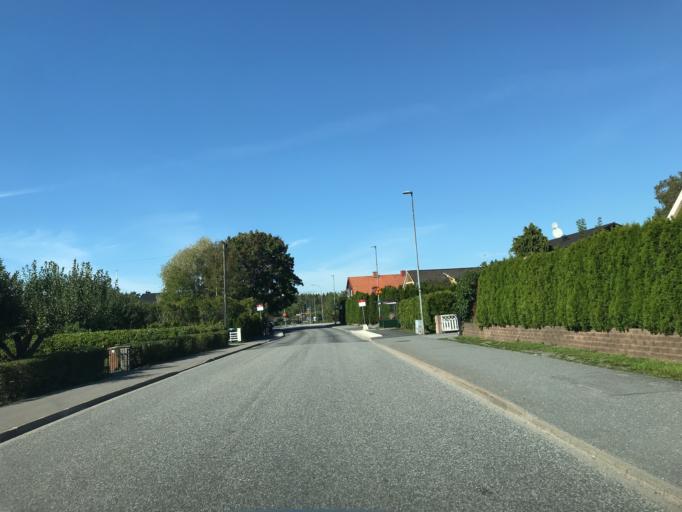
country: SE
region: Stockholm
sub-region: Sollentuna Kommun
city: Sollentuna
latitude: 59.4257
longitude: 17.9281
